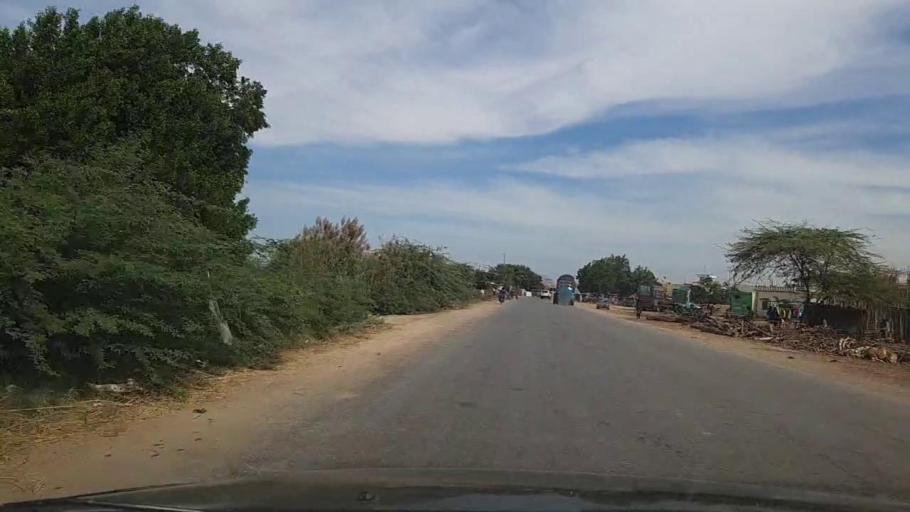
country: PK
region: Sindh
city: Thatta
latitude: 24.7911
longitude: 67.9564
